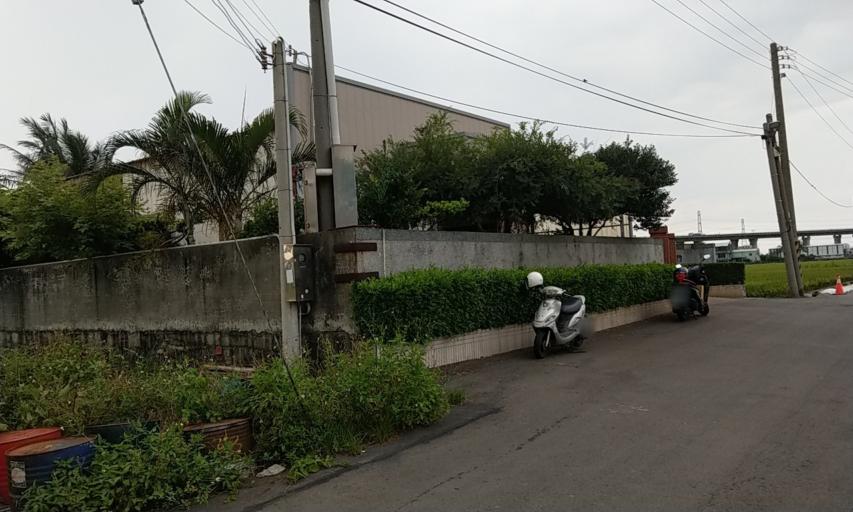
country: TW
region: Taiwan
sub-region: Changhua
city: Chang-hua
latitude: 24.1630
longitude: 120.5344
